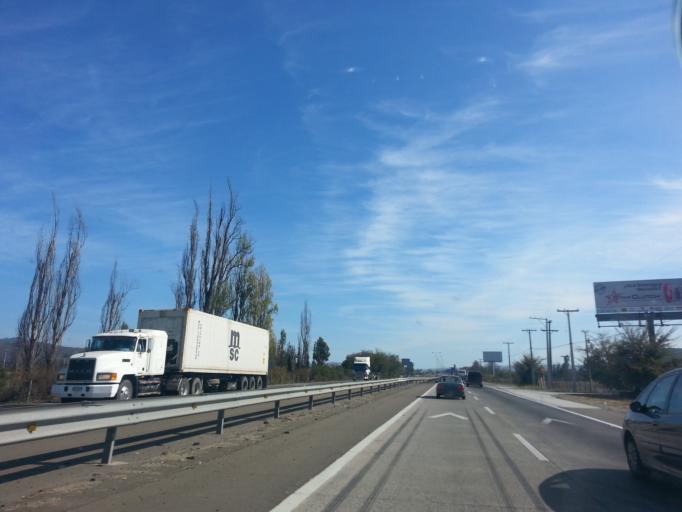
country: CL
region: Valparaiso
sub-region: Provincia de Marga Marga
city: Villa Alemana
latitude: -33.3360
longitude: -71.3763
